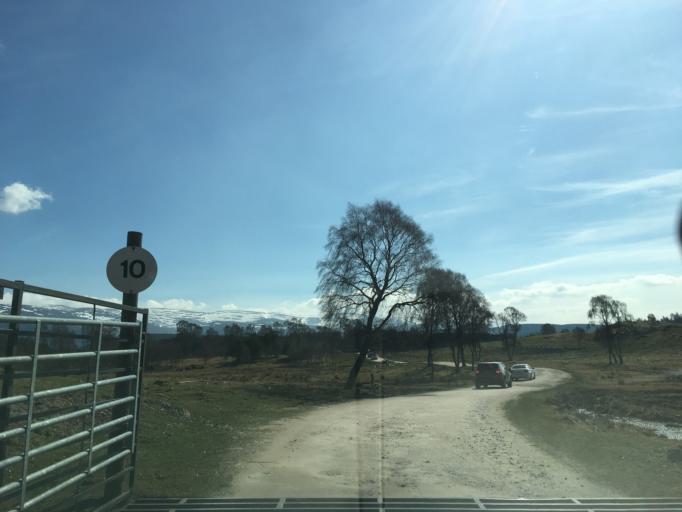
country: GB
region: Scotland
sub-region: Highland
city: Kingussie
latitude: 57.1137
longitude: -3.9794
